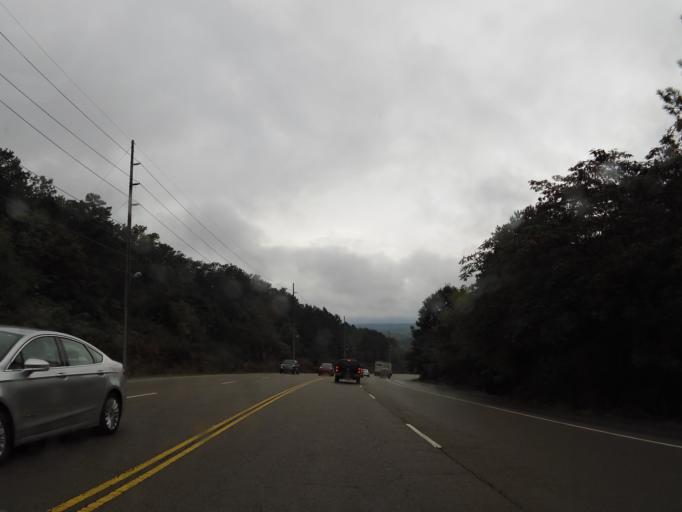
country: US
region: Tennessee
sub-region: Bradley County
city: Hopewell
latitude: 35.2130
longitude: -84.8771
